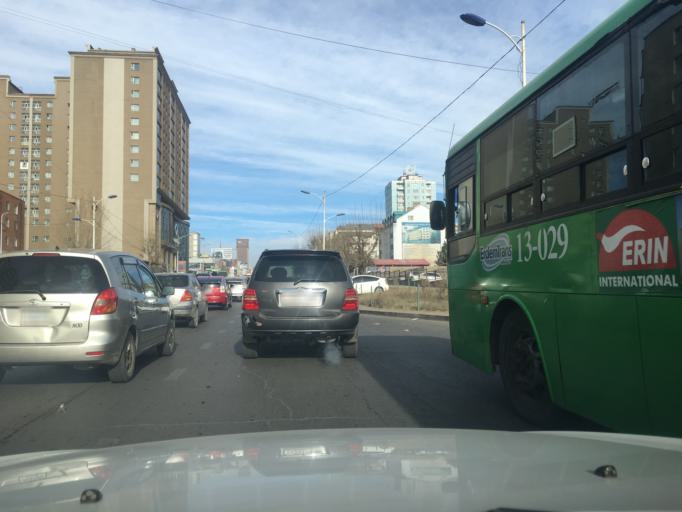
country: MN
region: Ulaanbaatar
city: Ulaanbaatar
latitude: 47.9154
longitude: 106.8765
